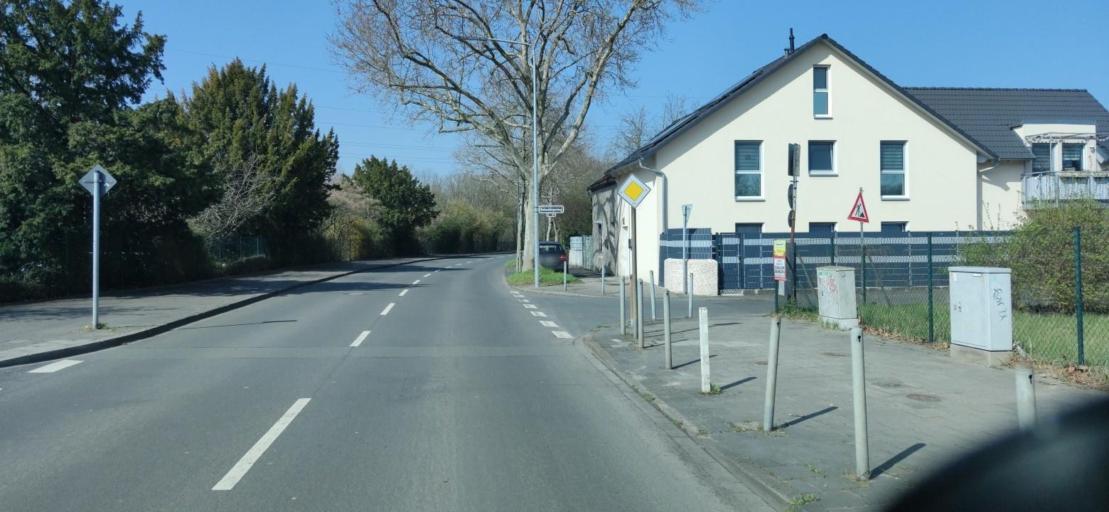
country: DE
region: North Rhine-Westphalia
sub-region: Regierungsbezirk Dusseldorf
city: Dusseldorf
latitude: 51.1831
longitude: 6.8357
